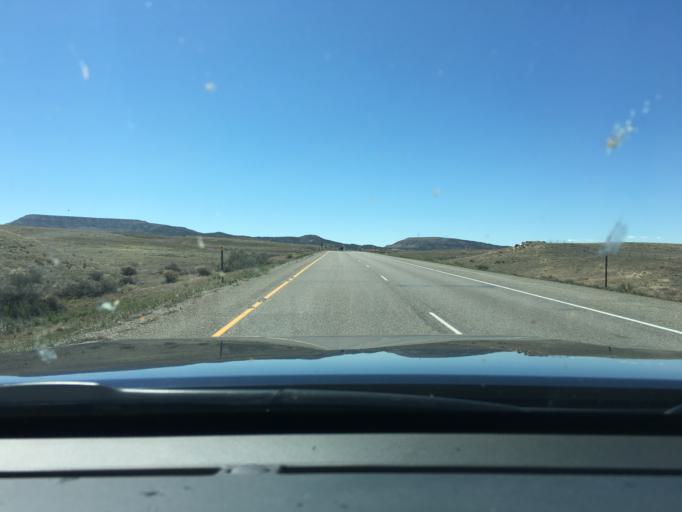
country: US
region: Colorado
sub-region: Mesa County
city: Loma
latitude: 39.2321
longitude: -108.9130
